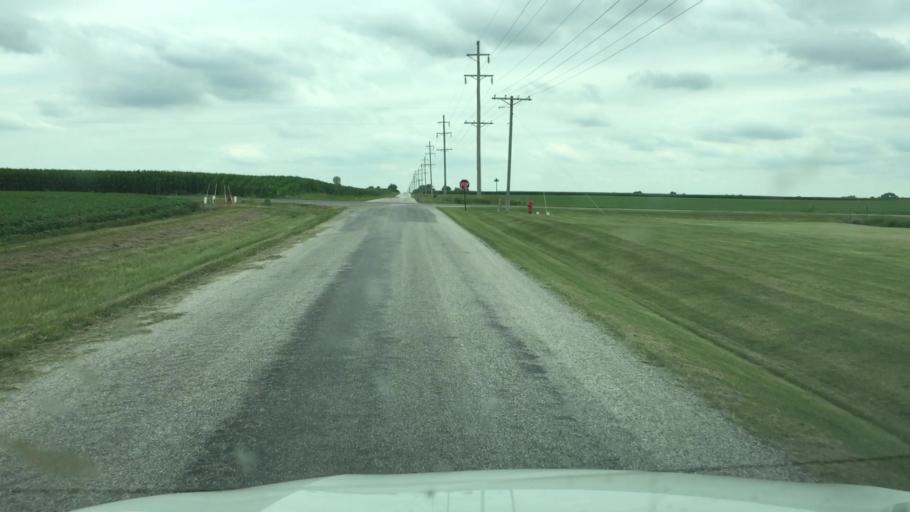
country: US
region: Illinois
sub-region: Hancock County
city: Carthage
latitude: 40.3424
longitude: -91.0823
